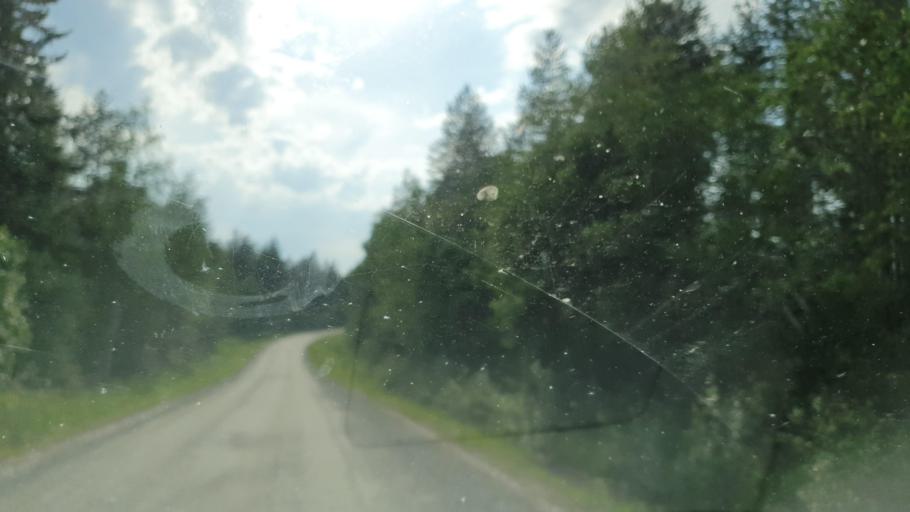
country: FI
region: Kainuu
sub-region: Kehys-Kainuu
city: Kuhmo
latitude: 64.0956
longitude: 29.6315
